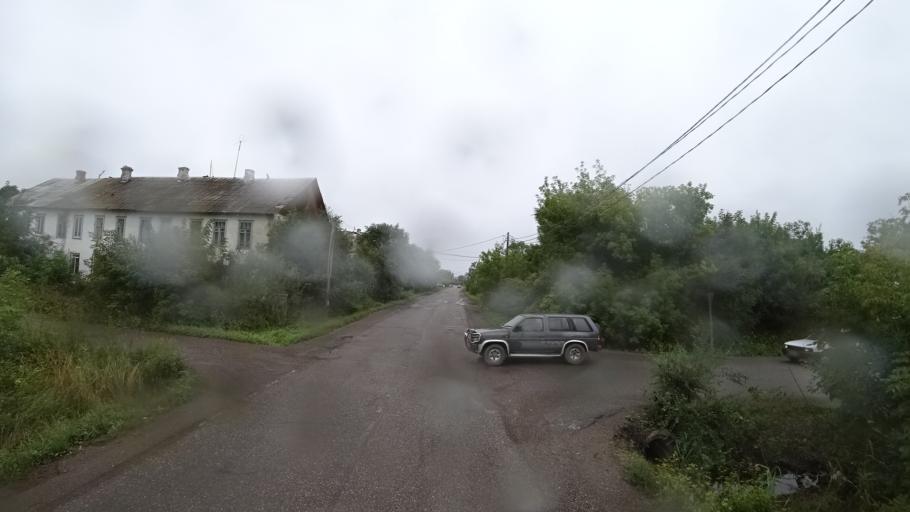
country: RU
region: Primorskiy
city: Monastyrishche
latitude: 44.1985
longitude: 132.4252
